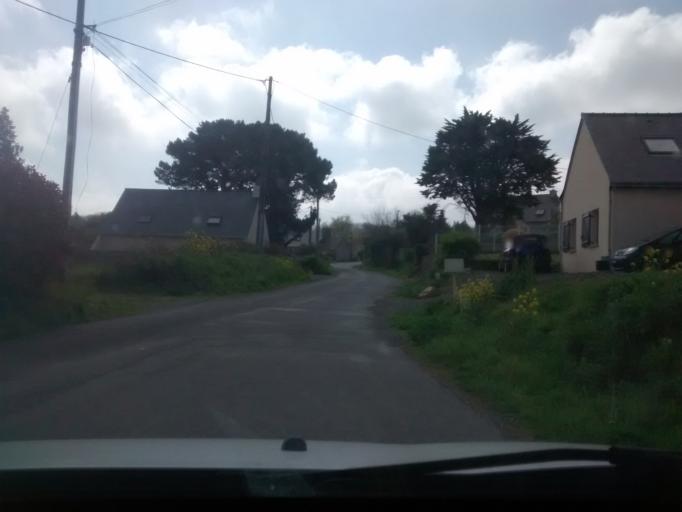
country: FR
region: Brittany
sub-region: Departement des Cotes-d'Armor
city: Trevou-Treguignec
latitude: 48.8296
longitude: -3.3202
